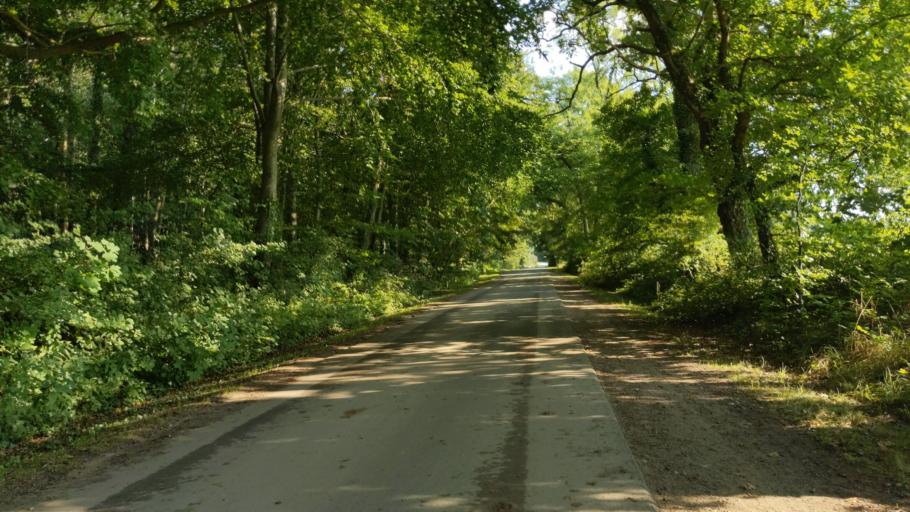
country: DE
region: Mecklenburg-Vorpommern
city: Kalkhorst
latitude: 54.0019
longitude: 11.0443
